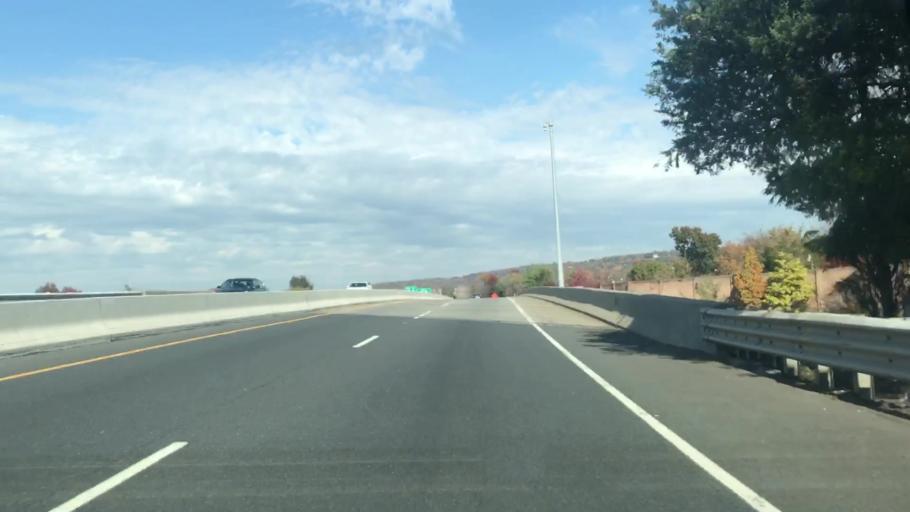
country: US
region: New Jersey
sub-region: Somerset County
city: Green Knoll
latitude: 40.5939
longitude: -74.6231
